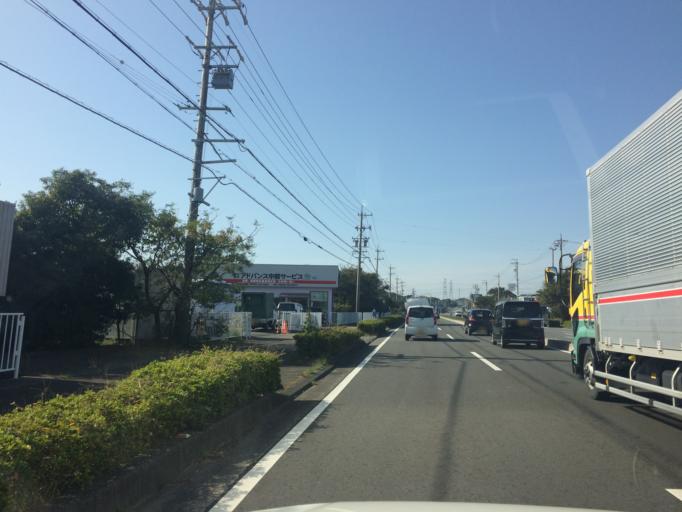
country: JP
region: Shizuoka
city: Oyama
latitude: 34.6235
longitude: 138.1639
